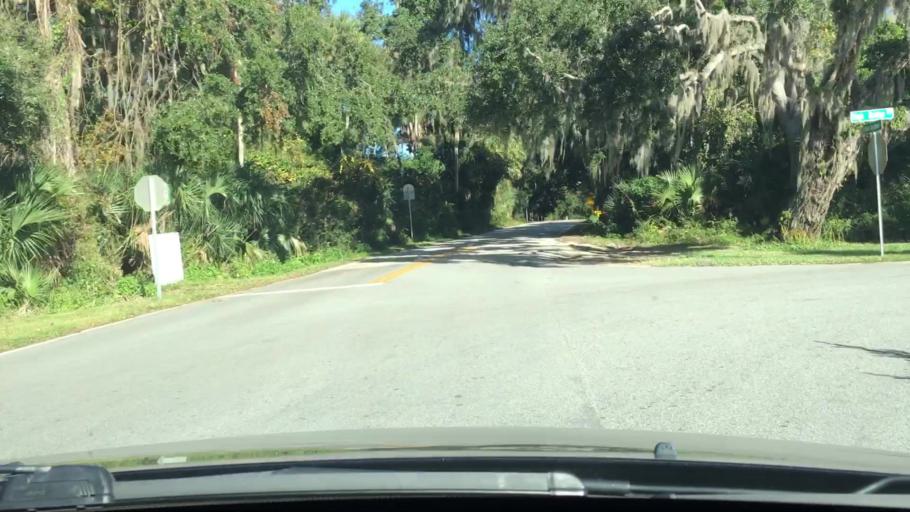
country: US
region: Florida
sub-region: Flagler County
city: Flagler Beach
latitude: 29.4092
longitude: -81.1194
